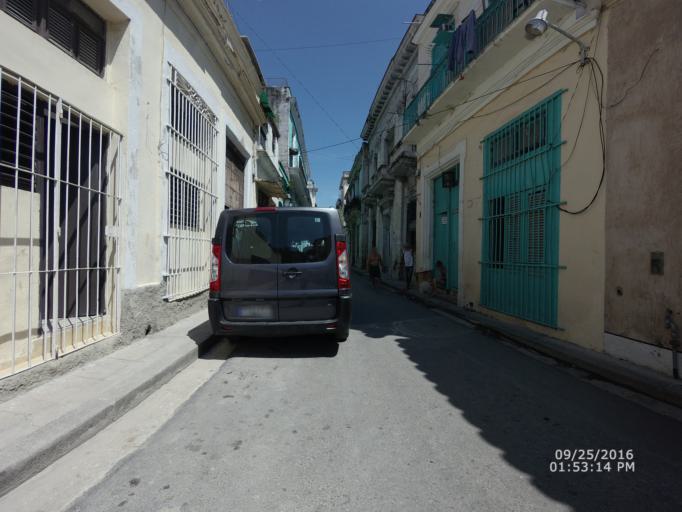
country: CU
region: La Habana
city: Centro Habana
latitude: 23.1411
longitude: -82.3560
